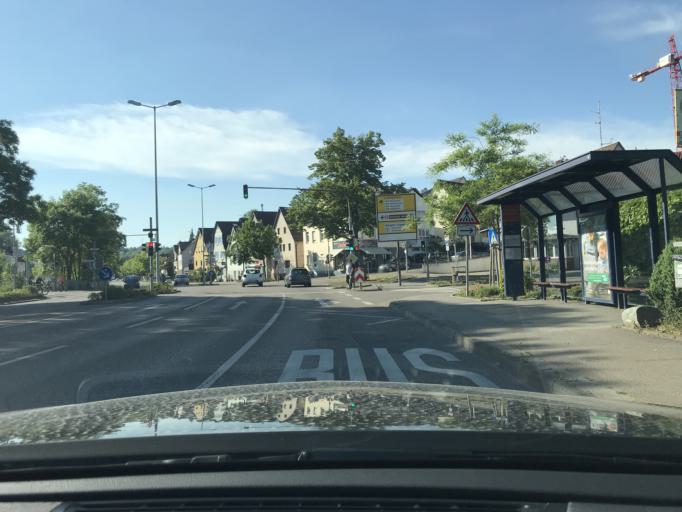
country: DE
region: Baden-Wuerttemberg
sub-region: Regierungsbezirk Stuttgart
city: Waiblingen
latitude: 48.8331
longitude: 9.3210
